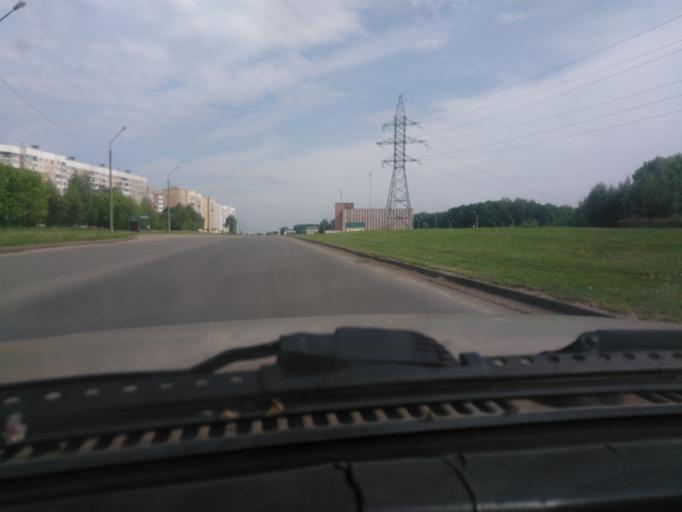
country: BY
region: Mogilev
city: Mahilyow
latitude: 53.9462
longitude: 30.3591
